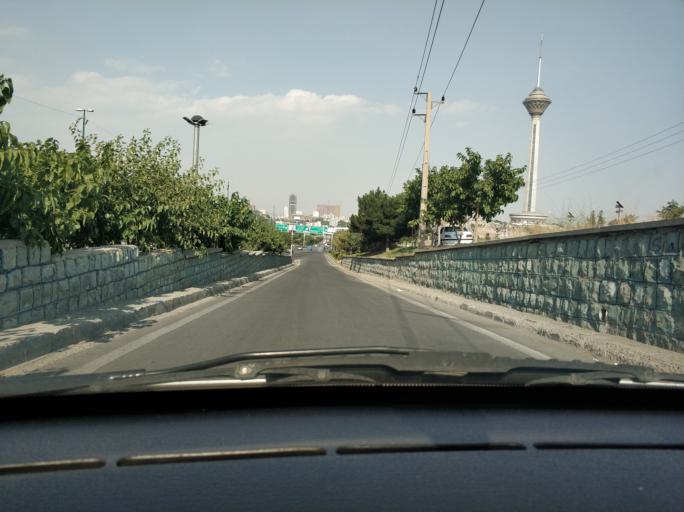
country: IR
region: Tehran
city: Tehran
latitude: 35.7493
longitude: 51.3619
